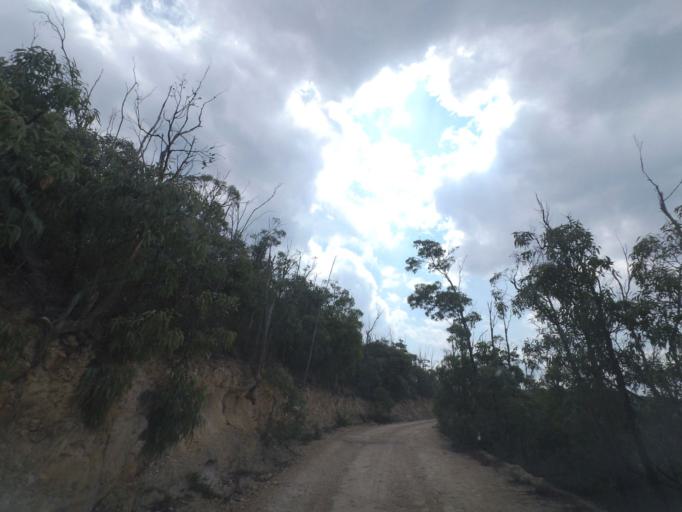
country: AU
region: Victoria
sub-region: Moorabool
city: Bacchus Marsh
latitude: -37.5604
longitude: 144.4254
